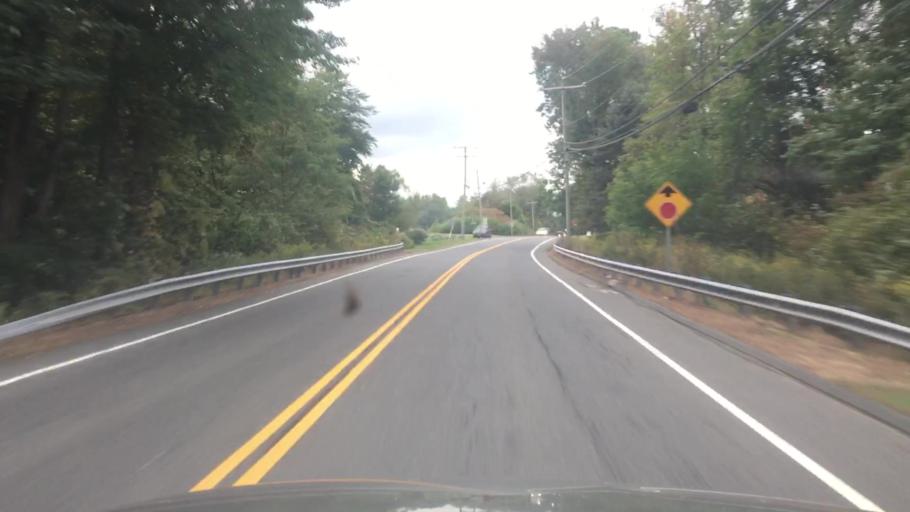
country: US
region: Connecticut
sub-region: Tolland County
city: Somers
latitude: 42.0129
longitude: -72.4824
